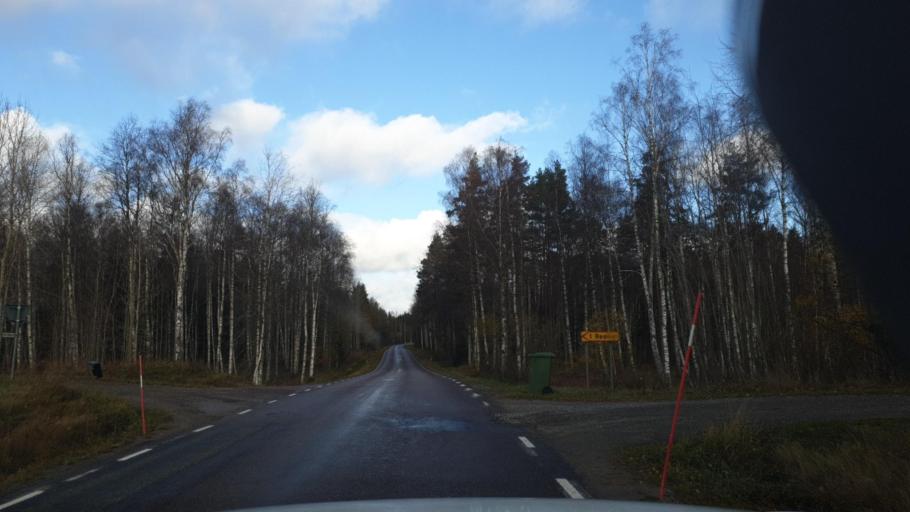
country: SE
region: Vaermland
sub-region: Grums Kommun
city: Slottsbron
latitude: 59.4818
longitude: 12.8834
